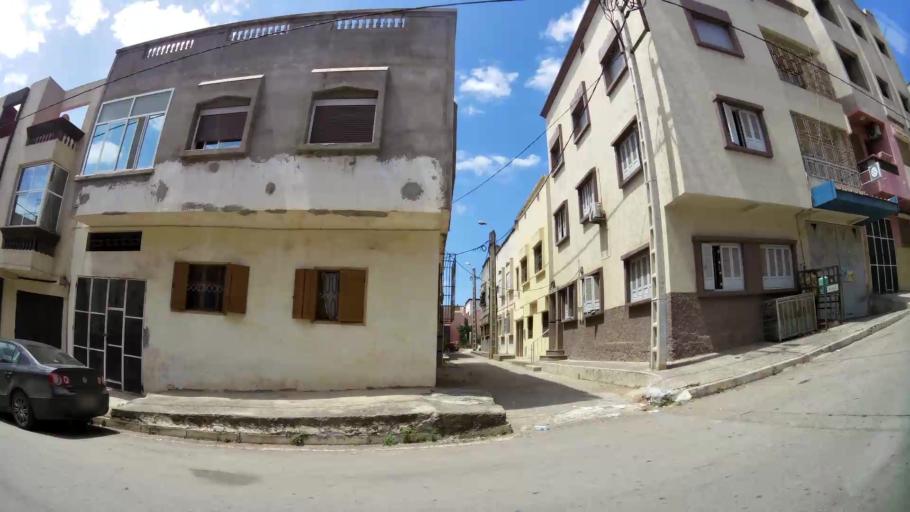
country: MA
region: Gharb-Chrarda-Beni Hssen
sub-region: Kenitra Province
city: Kenitra
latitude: 34.2741
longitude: -6.6010
